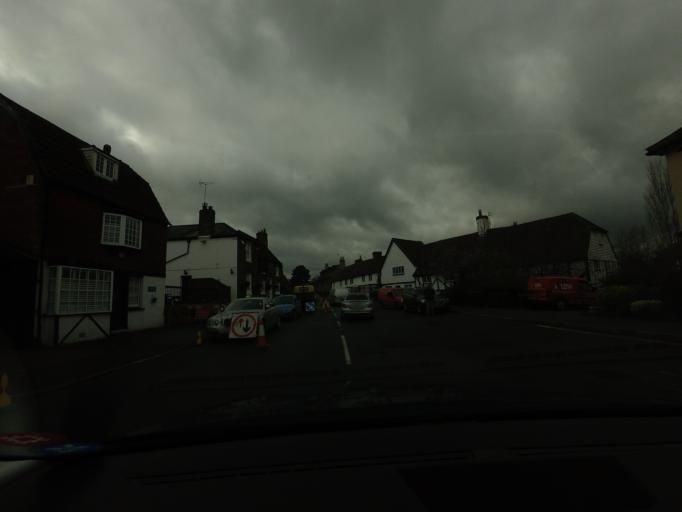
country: GB
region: England
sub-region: Kent
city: Eynsford
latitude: 51.3693
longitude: 0.2141
